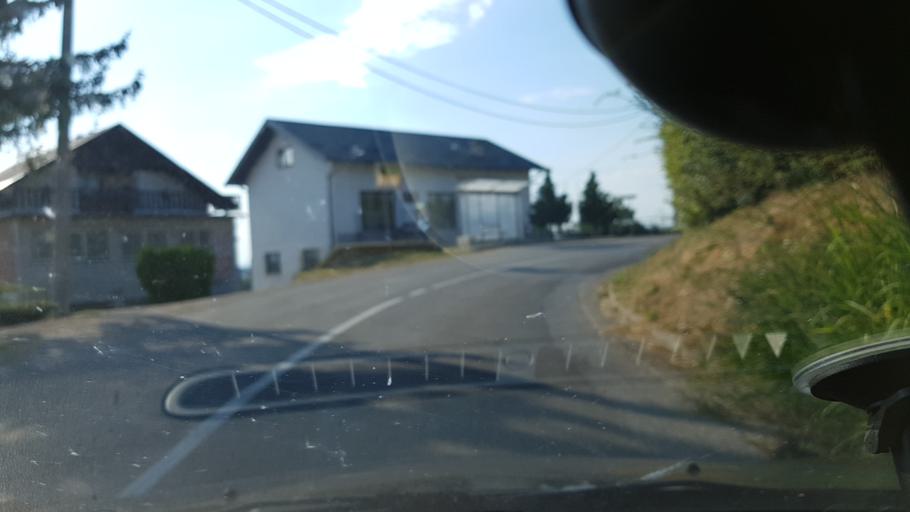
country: HR
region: Zagrebacka
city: Bregana
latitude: 45.9033
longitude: 15.6838
